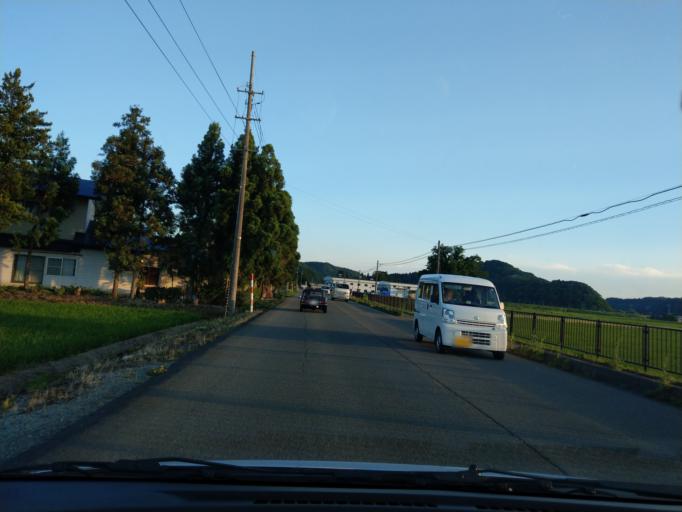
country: JP
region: Akita
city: Kakunodatemachi
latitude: 39.6183
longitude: 140.5717
